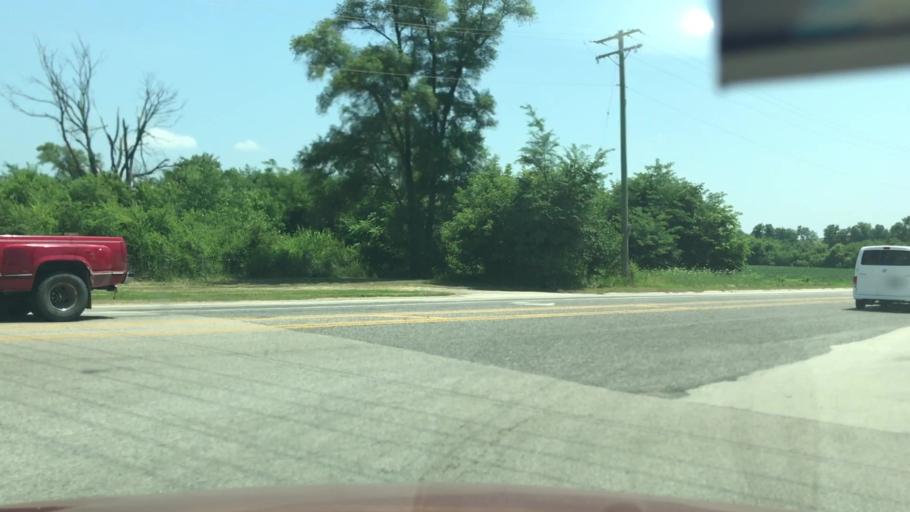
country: US
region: Illinois
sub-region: Winnebago County
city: Cherry Valley
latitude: 42.2397
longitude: -88.9007
